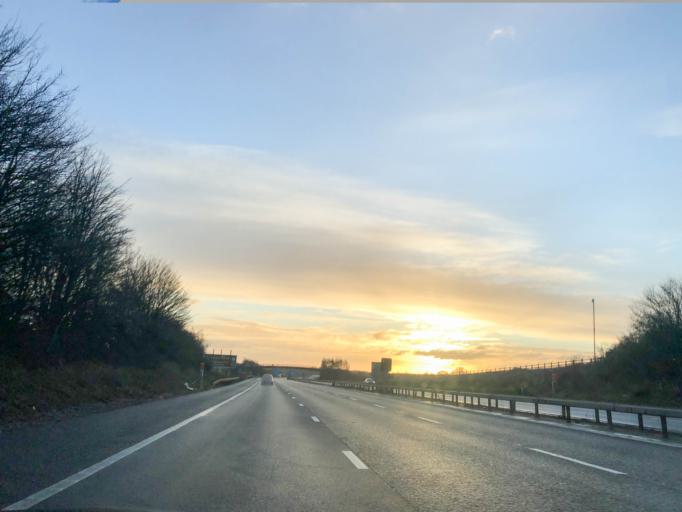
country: GB
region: England
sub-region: Warwickshire
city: Warwick
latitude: 52.2648
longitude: -1.6288
